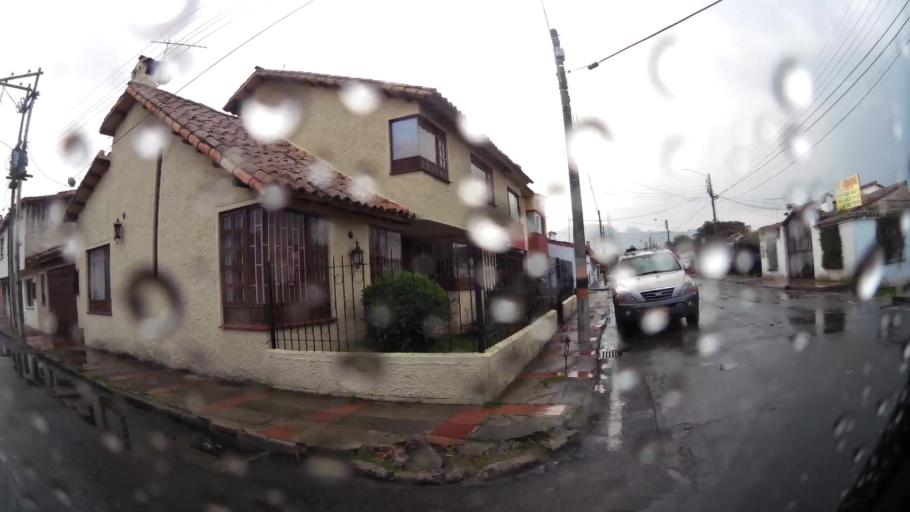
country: CO
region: Cundinamarca
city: Chia
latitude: 4.8586
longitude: -74.0556
